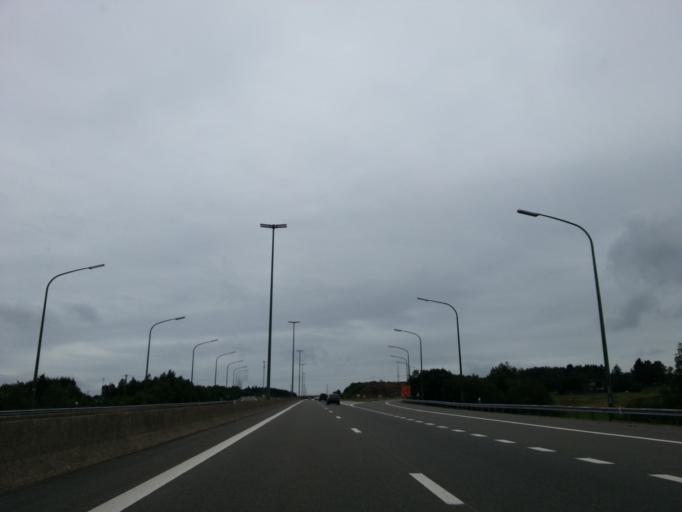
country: BE
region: Wallonia
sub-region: Province de Liege
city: Malmedy
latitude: 50.4754
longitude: 5.9720
